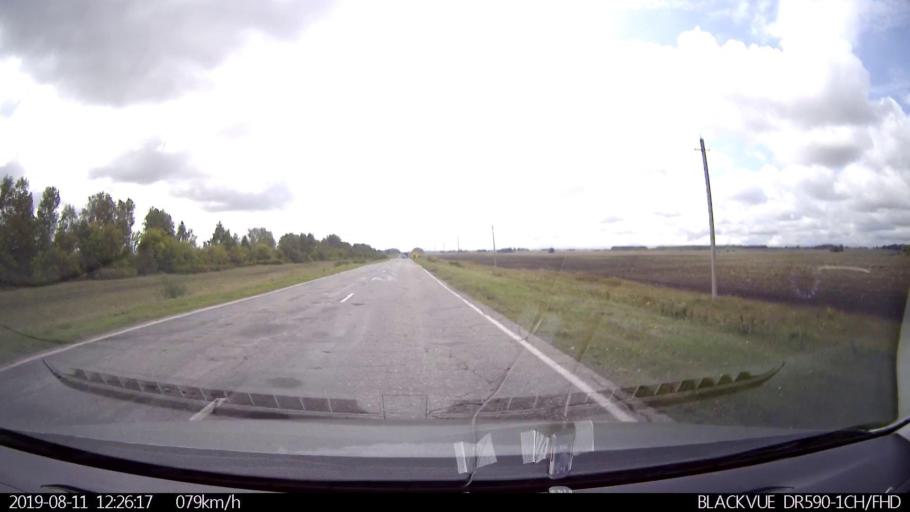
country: RU
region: Ulyanovsk
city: Ignatovka
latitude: 53.8653
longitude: 47.9320
